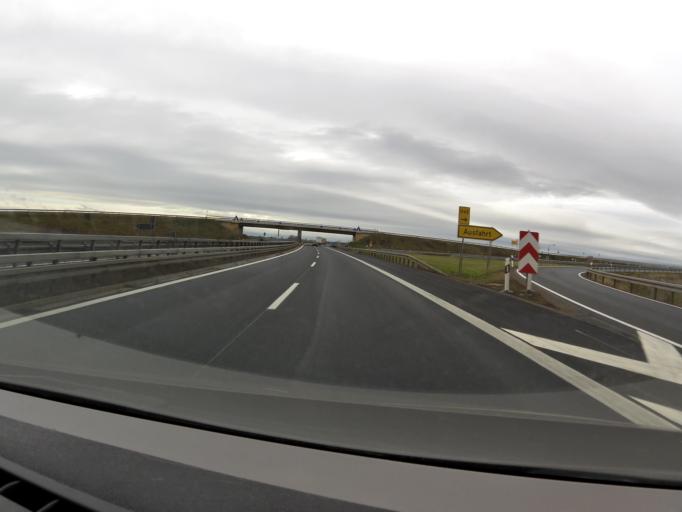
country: DE
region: Saxony-Anhalt
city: Ilberstedt
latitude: 51.8104
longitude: 11.6492
